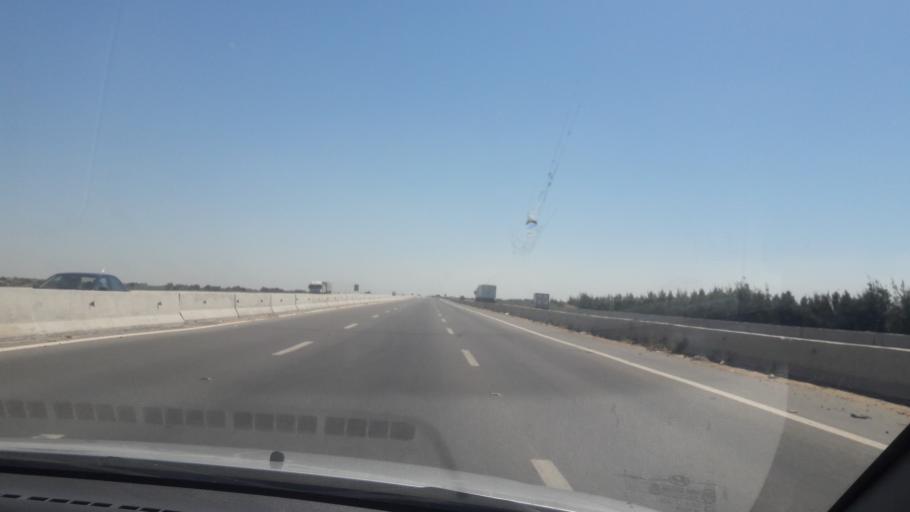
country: EG
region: Muhafazat ad Daqahliyah
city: Al Matariyah
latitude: 30.9086
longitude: 32.1861
